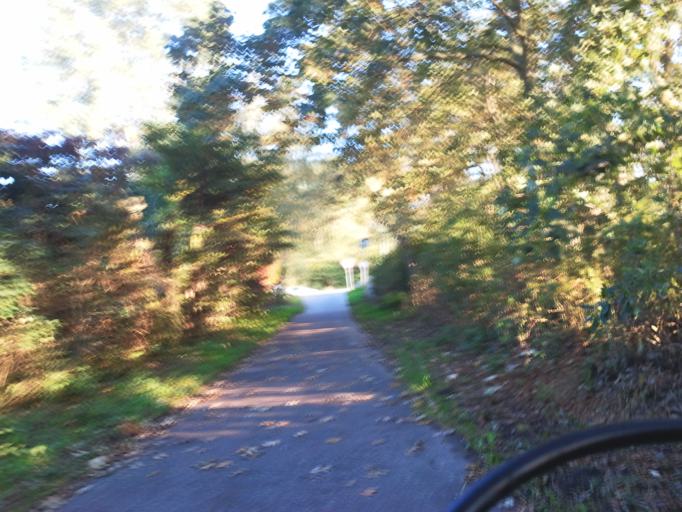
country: DE
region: Mecklenburg-Vorpommern
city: Kritzmow
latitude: 54.0841
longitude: 12.0711
